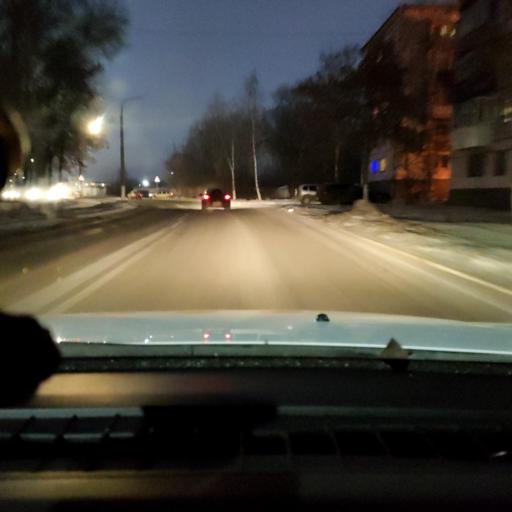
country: RU
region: Samara
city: Chapayevsk
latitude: 52.9635
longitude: 49.6915
